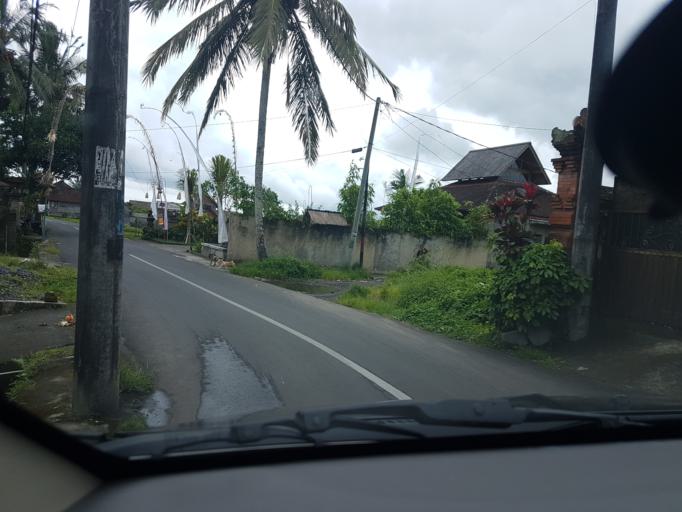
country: ID
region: Bali
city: Banjar Triwangsakeliki
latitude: -8.4581
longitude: 115.2746
